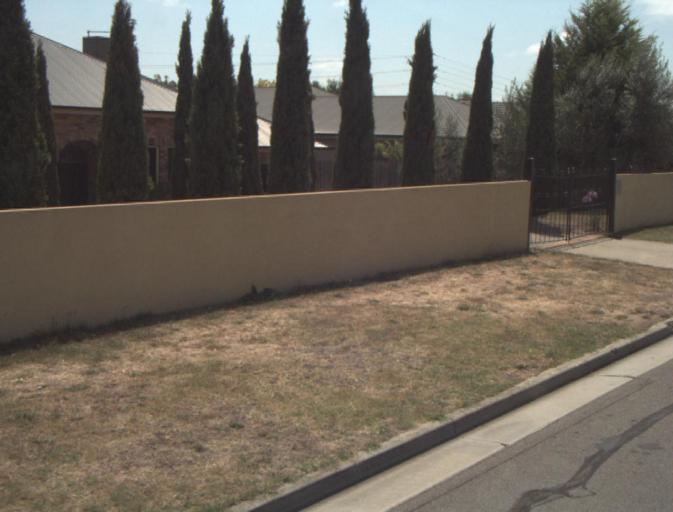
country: AU
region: Tasmania
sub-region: Launceston
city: Newstead
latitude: -41.4816
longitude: 147.1799
